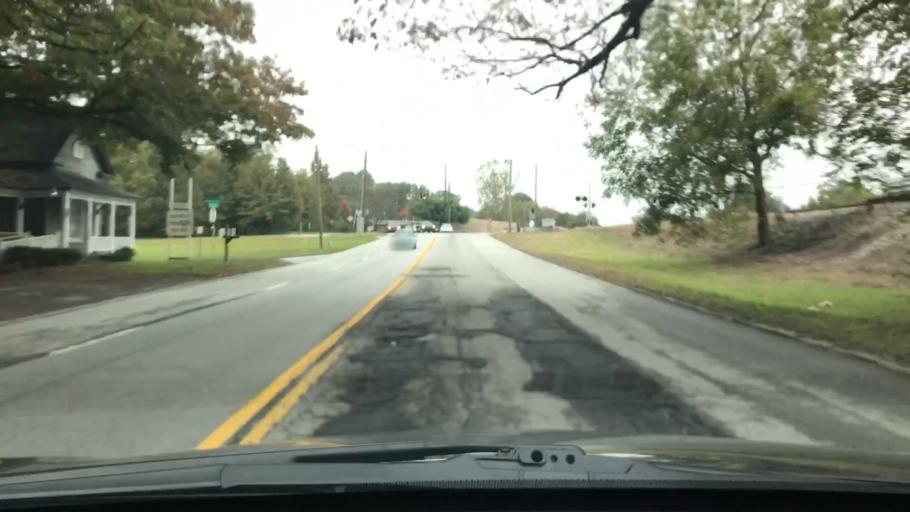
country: US
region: Georgia
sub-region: DeKalb County
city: Scottdale
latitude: 33.7890
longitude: -84.2647
